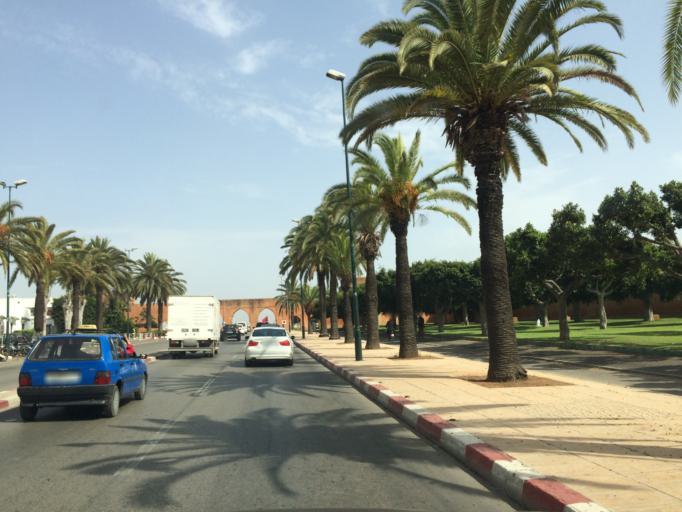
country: MA
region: Rabat-Sale-Zemmour-Zaer
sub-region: Rabat
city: Rabat
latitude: 34.0072
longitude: -6.8276
